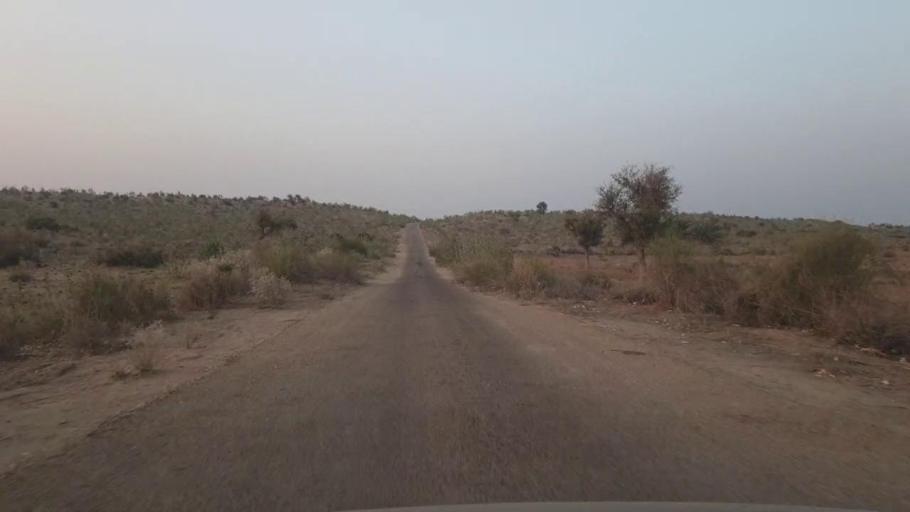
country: PK
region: Sindh
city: Umarkot
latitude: 25.2764
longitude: 70.0769
